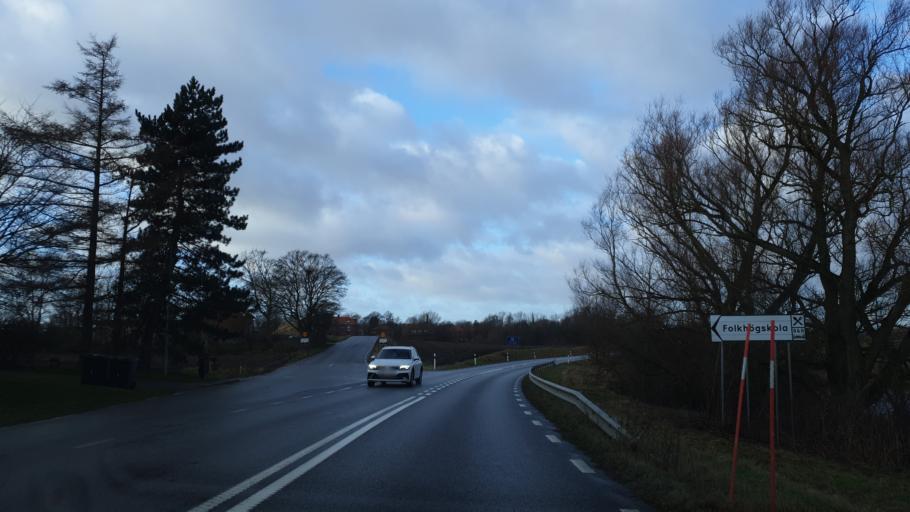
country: SE
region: Skane
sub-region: Malmo
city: Oxie
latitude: 55.4635
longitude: 13.1461
